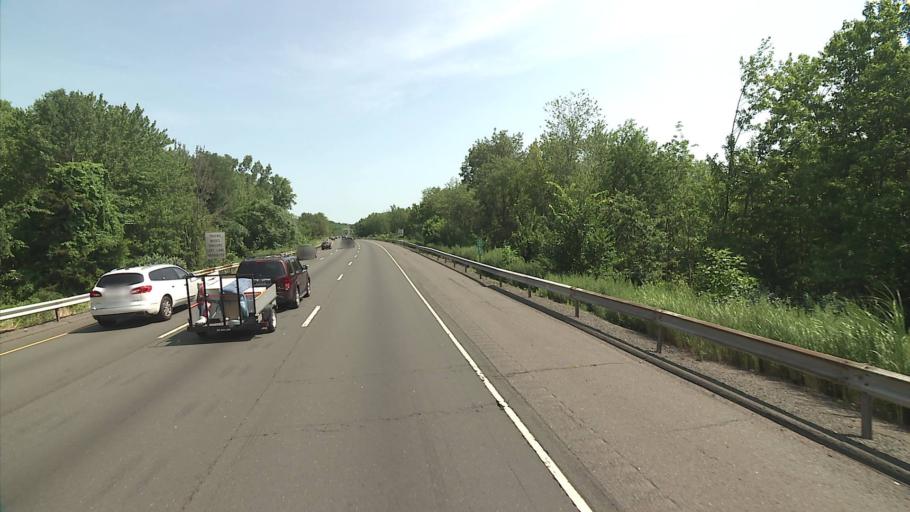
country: US
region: Connecticut
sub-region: Middlesex County
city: Cromwell
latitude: 41.6125
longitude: -72.6983
